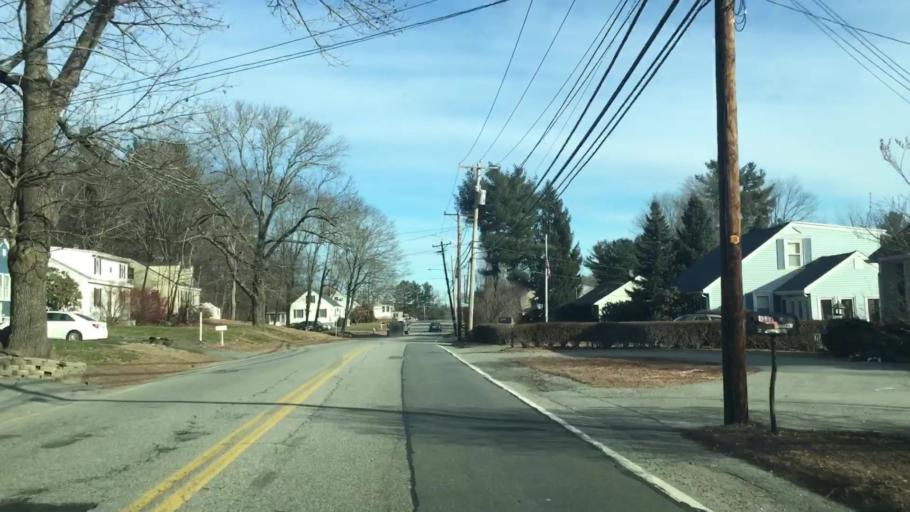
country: US
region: New Hampshire
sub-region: Hillsborough County
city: Pelham
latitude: 42.6890
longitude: -71.3537
